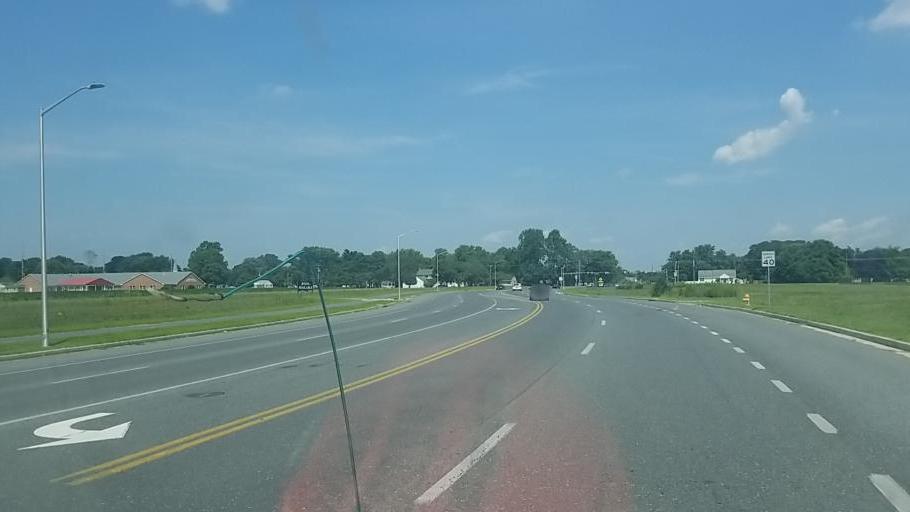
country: US
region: Maryland
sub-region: Wicomico County
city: Salisbury
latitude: 38.3710
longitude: -75.5591
